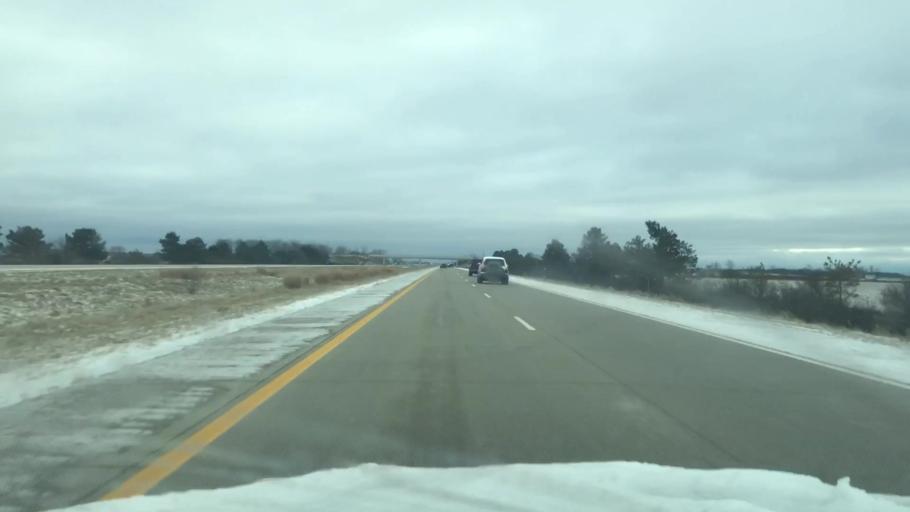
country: US
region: Michigan
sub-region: Bay County
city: Pinconning
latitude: 43.7786
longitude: -84.0254
